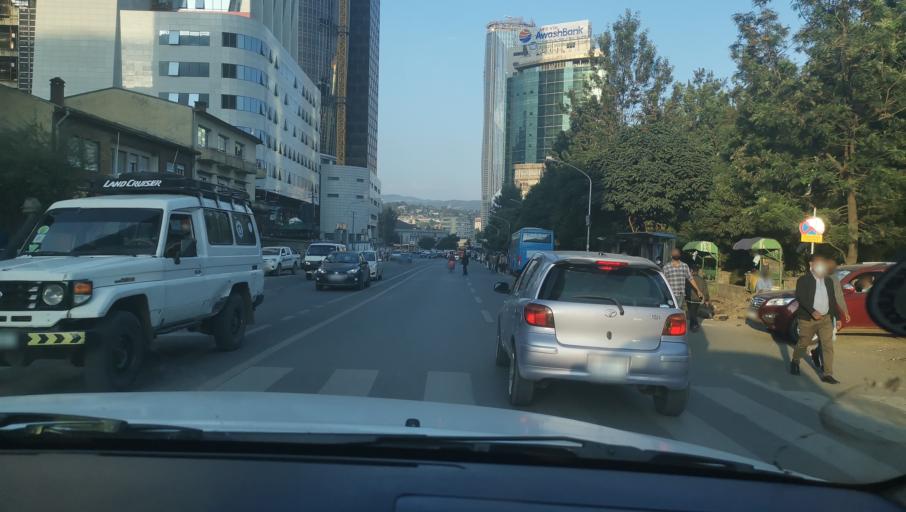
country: ET
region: Adis Abeba
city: Addis Ababa
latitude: 9.0135
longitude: 38.7492
